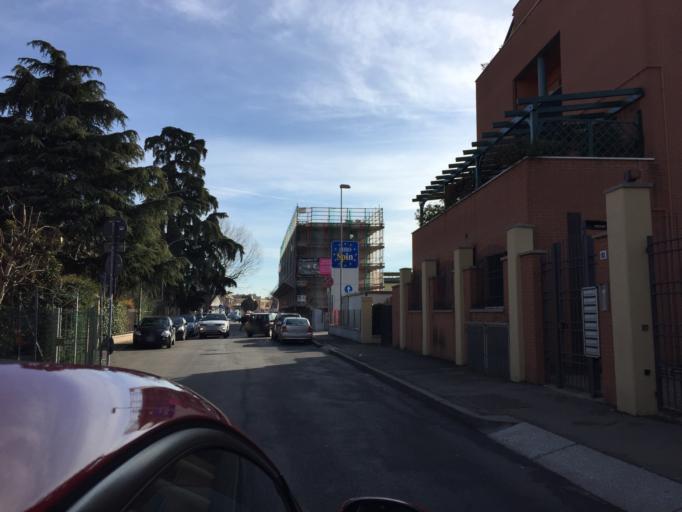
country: IT
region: Emilia-Romagna
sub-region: Provincia di Bologna
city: Bologna
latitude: 44.5041
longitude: 11.3020
